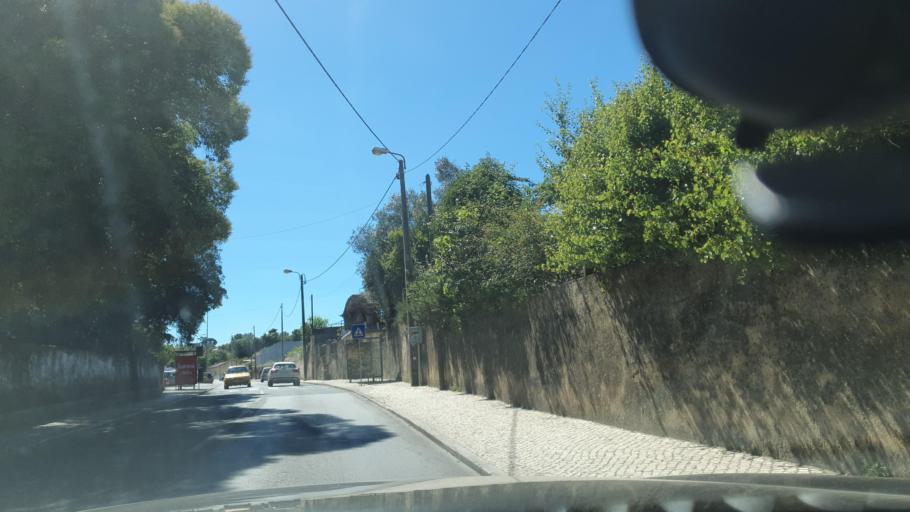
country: PT
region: Lisbon
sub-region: Sintra
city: Belas
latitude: 38.7762
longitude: -9.2680
